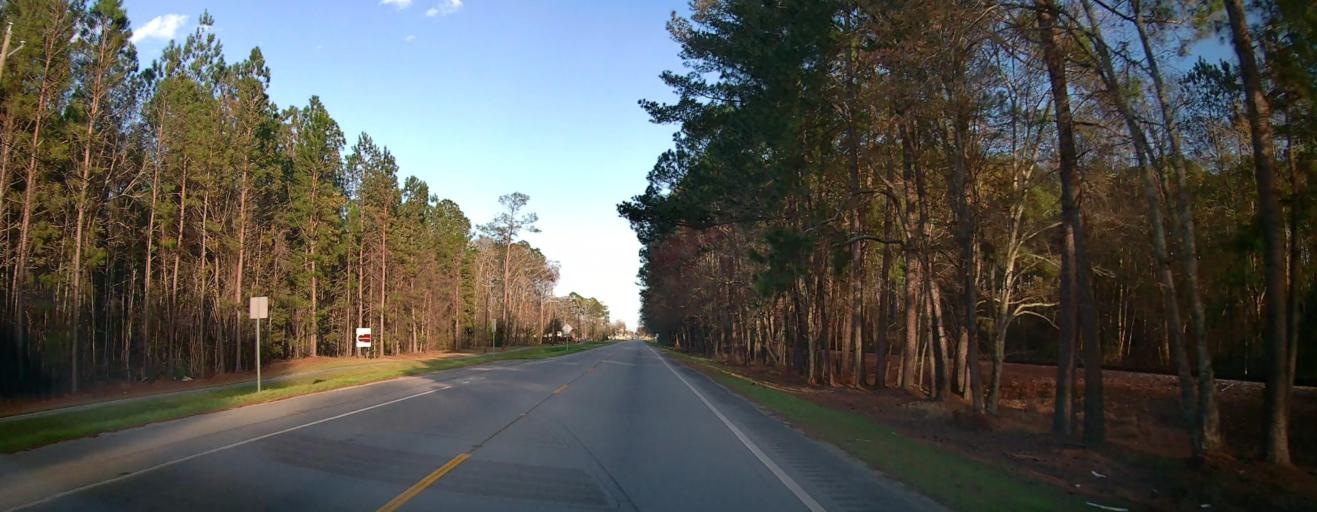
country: US
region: Georgia
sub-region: Bryan County
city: Pembroke
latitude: 32.1366
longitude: -81.6355
